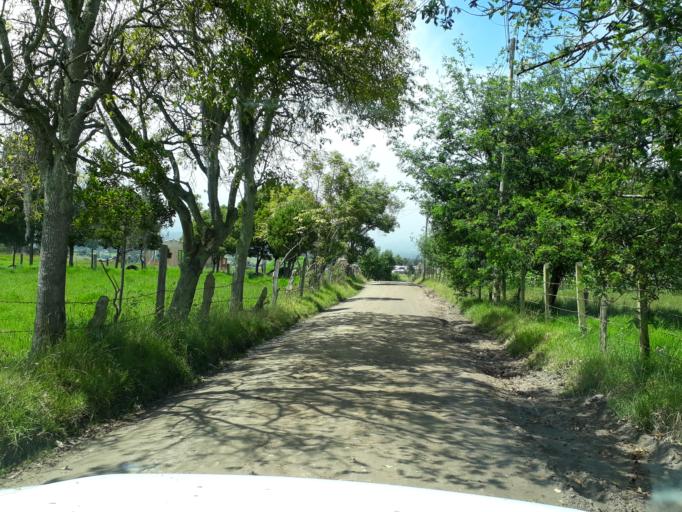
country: CO
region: Cundinamarca
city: Guasca
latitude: 4.8766
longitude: -73.8809
